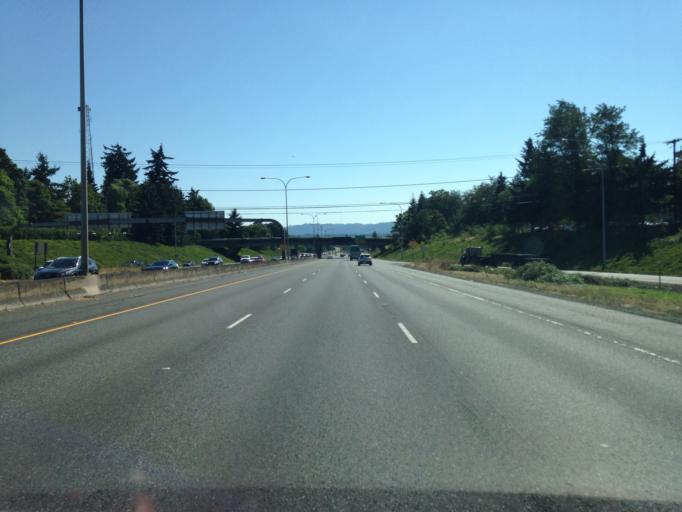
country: US
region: Washington
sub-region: Clark County
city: Vancouver
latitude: 45.6309
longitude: -122.6655
